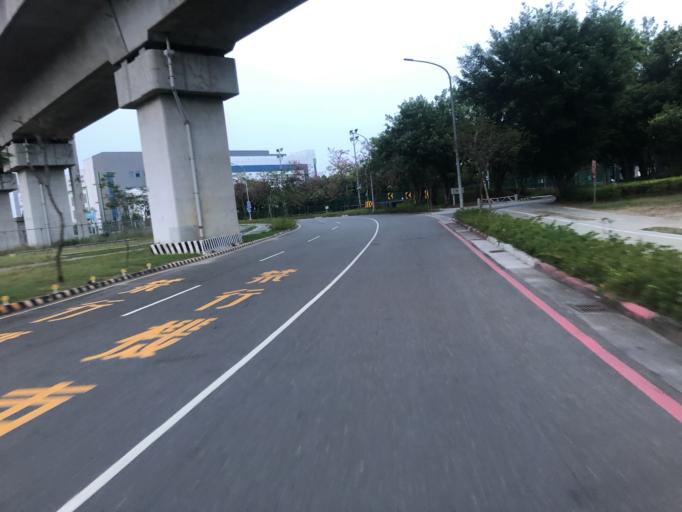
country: TW
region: Taiwan
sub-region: Tainan
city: Tainan
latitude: 23.0950
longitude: 120.2860
